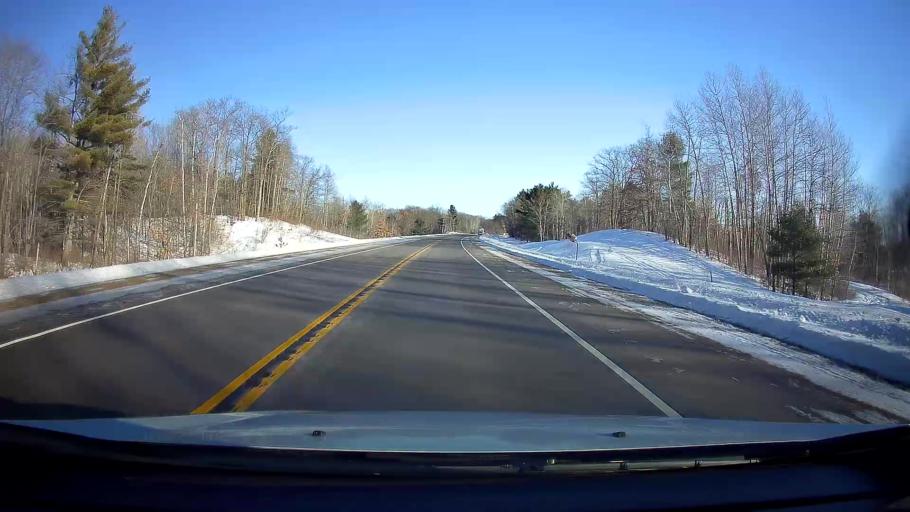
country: US
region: Wisconsin
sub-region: Sawyer County
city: Hayward
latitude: 46.0611
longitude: -91.4397
